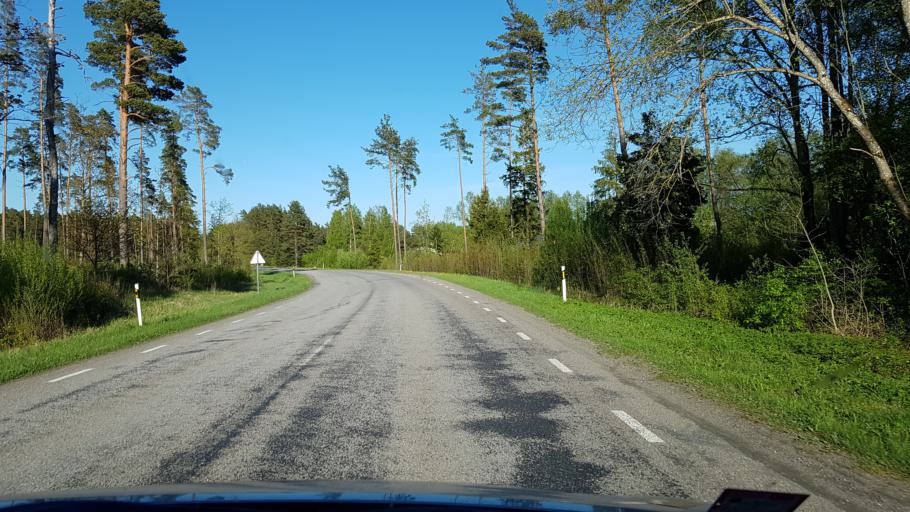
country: EE
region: Paernumaa
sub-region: Audru vald
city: Audru
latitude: 58.4073
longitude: 24.3257
